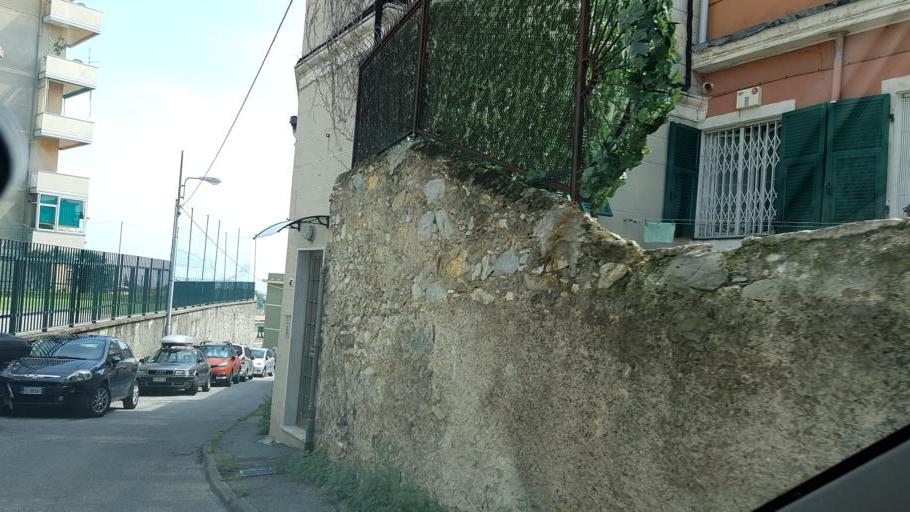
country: IT
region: Liguria
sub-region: Provincia di Genova
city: Genoa
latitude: 44.4069
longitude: 8.9819
